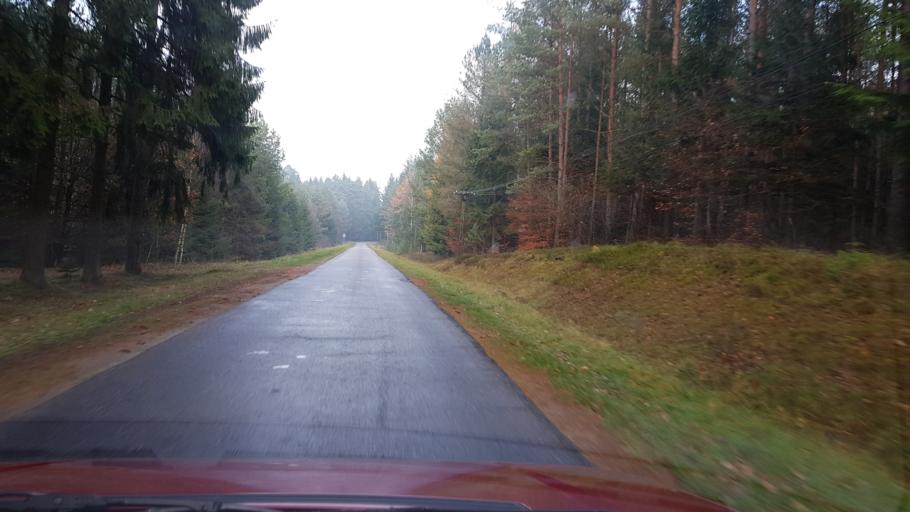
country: PL
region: West Pomeranian Voivodeship
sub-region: Powiat bialogardzki
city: Tychowo
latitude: 53.9545
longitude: 16.3158
